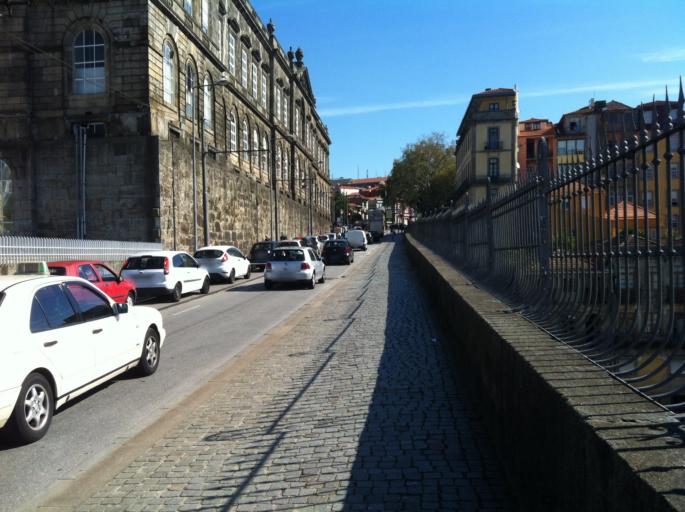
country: PT
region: Porto
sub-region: Porto
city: Porto
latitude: 41.1461
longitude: -8.6192
